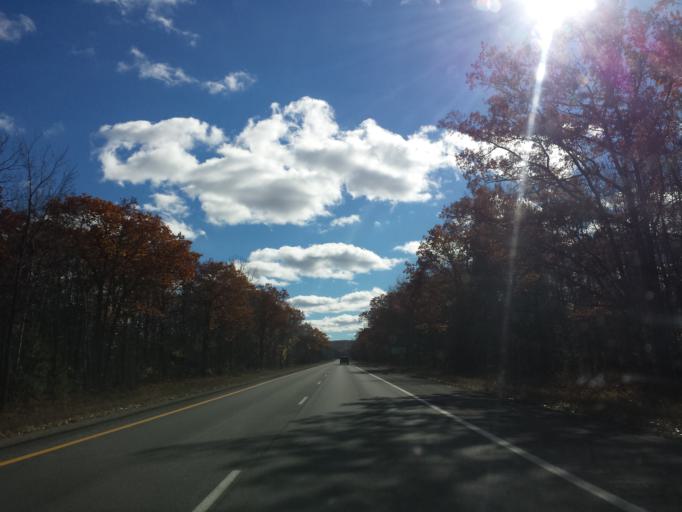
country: US
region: Michigan
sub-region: Cheboygan County
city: Indian River
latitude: 45.3894
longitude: -84.6072
